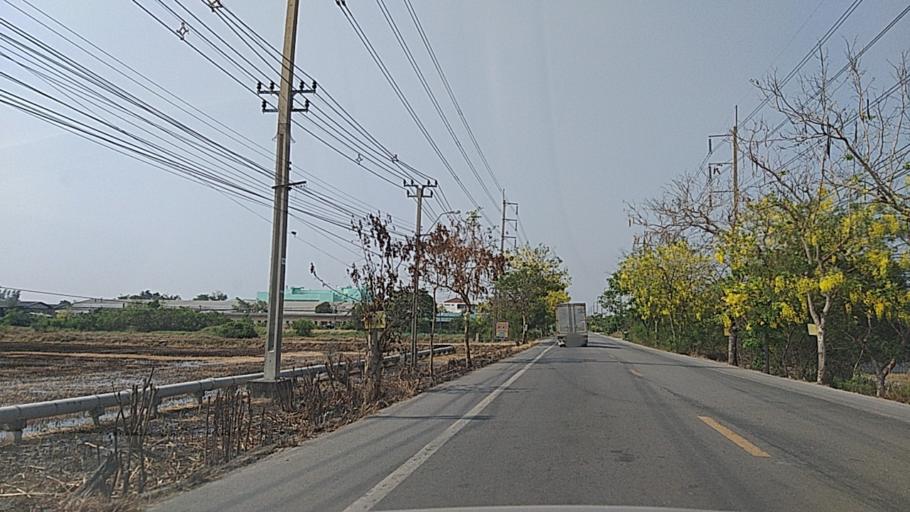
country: TH
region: Nonthaburi
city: Sai Noi
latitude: 14.0408
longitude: 100.3121
